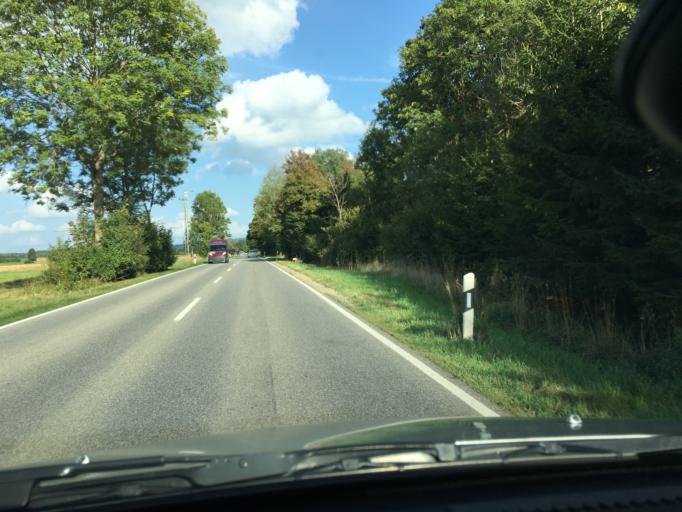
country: DE
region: Baden-Wuerttemberg
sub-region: Tuebingen Region
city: Ingoldingen
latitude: 48.0275
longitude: 9.7478
